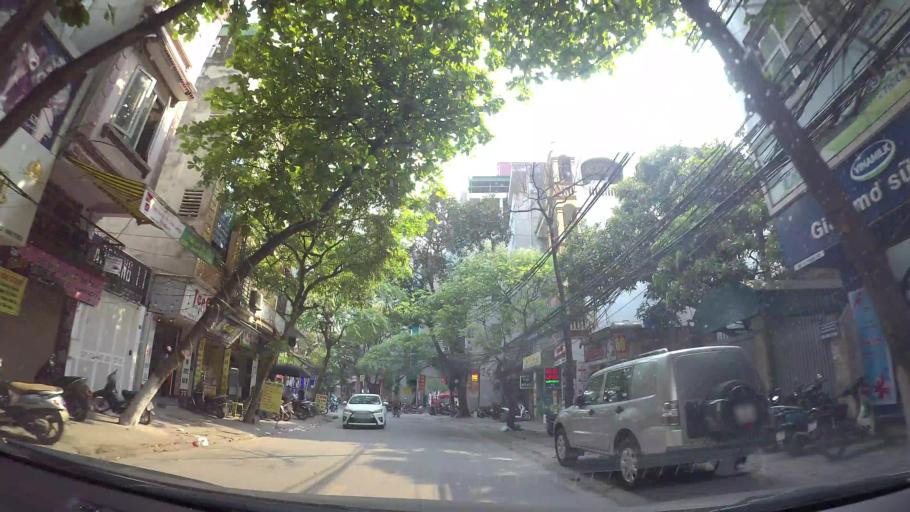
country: VN
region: Ha Noi
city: Dong Da
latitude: 20.9997
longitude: 105.8218
